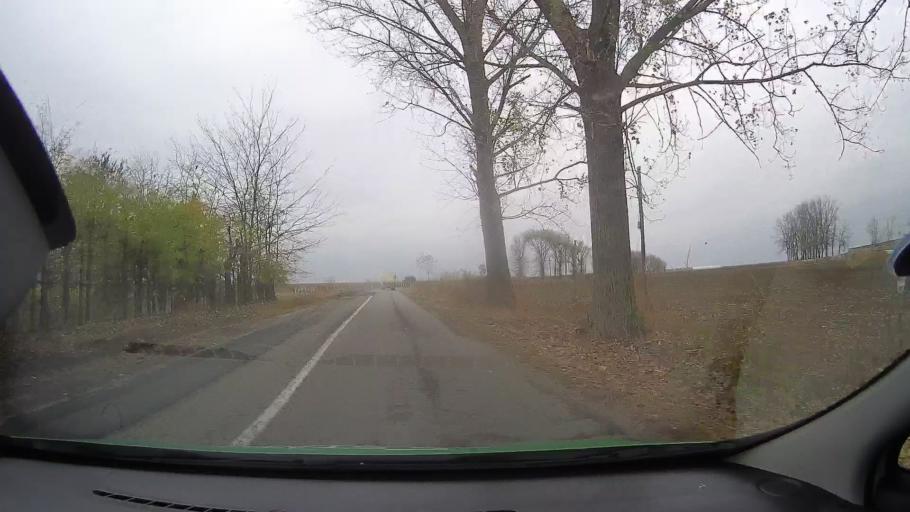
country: RO
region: Constanta
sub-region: Comuna Mihail Kogalniceanu
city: Mihail Kogalniceanu
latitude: 44.3814
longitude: 28.4625
